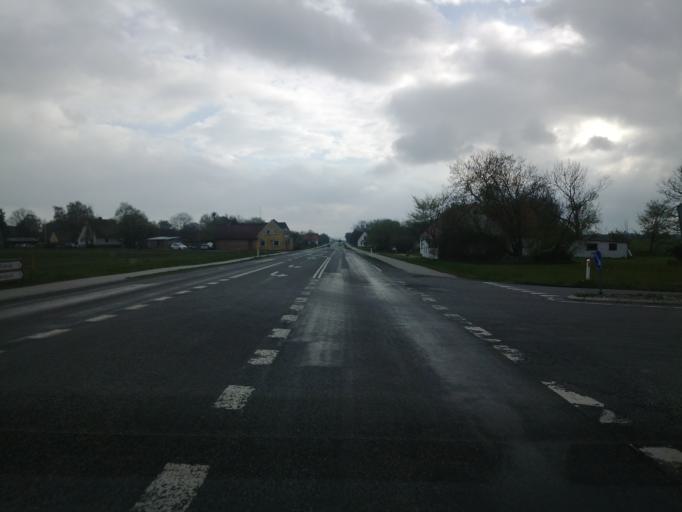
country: DK
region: North Denmark
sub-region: Frederikshavn Kommune
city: Saeby
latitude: 57.2907
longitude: 10.3864
